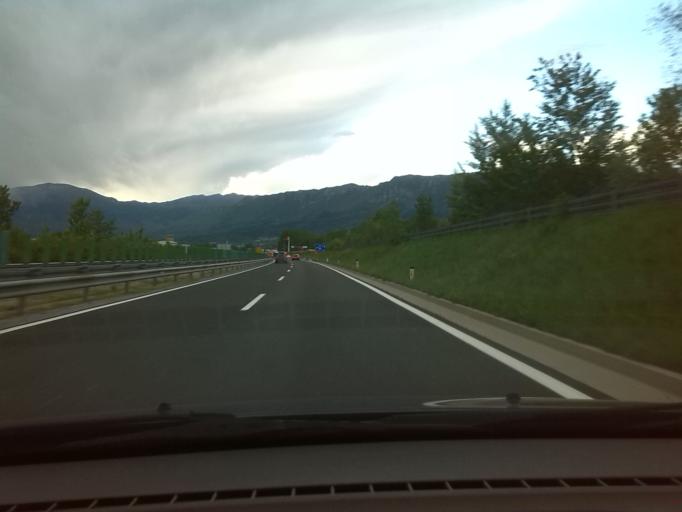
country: SI
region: Vipava
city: Vipava
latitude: 45.8249
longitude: 13.9604
